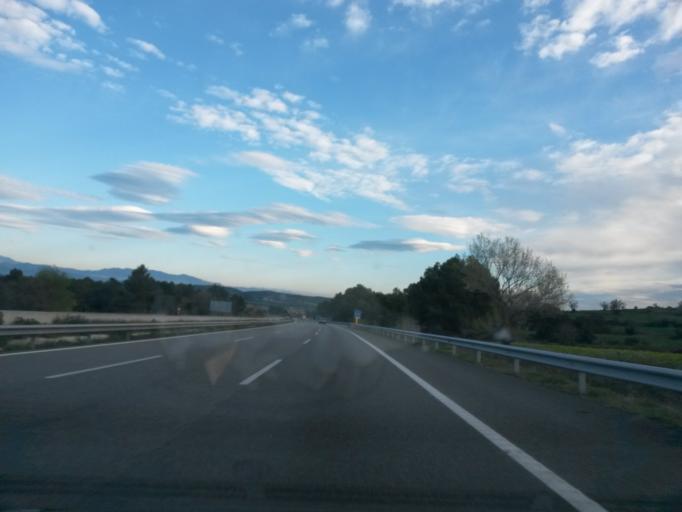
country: ES
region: Catalonia
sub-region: Provincia de Girona
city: Bascara
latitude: 42.1473
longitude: 2.9189
